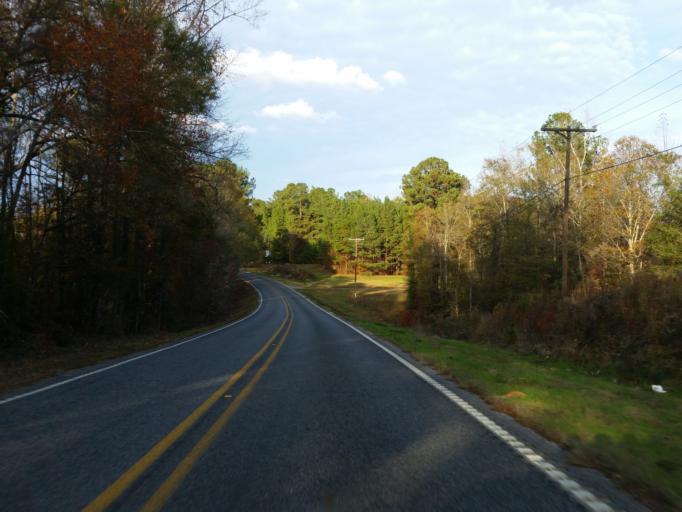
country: US
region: Mississippi
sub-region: Clarke County
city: Stonewall
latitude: 32.2216
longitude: -88.7745
